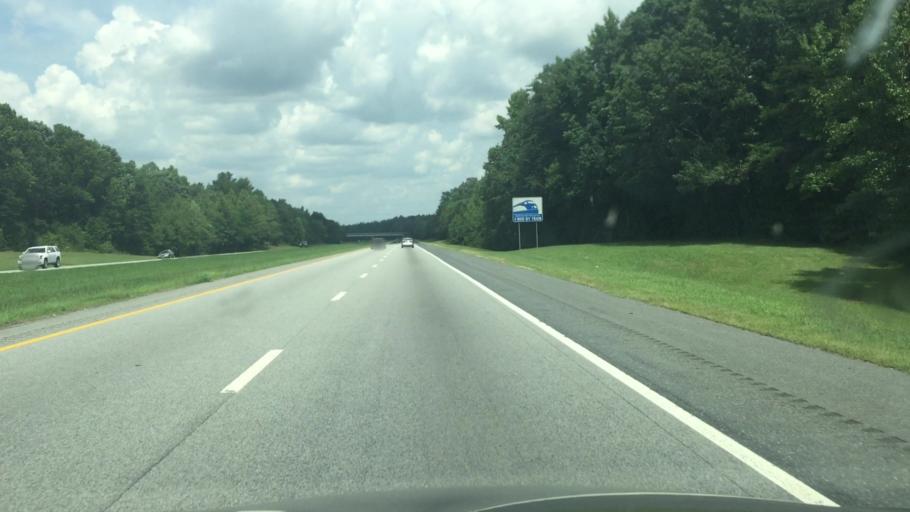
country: US
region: North Carolina
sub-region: Guilford County
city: Pleasant Garden
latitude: 35.9448
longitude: -79.8240
